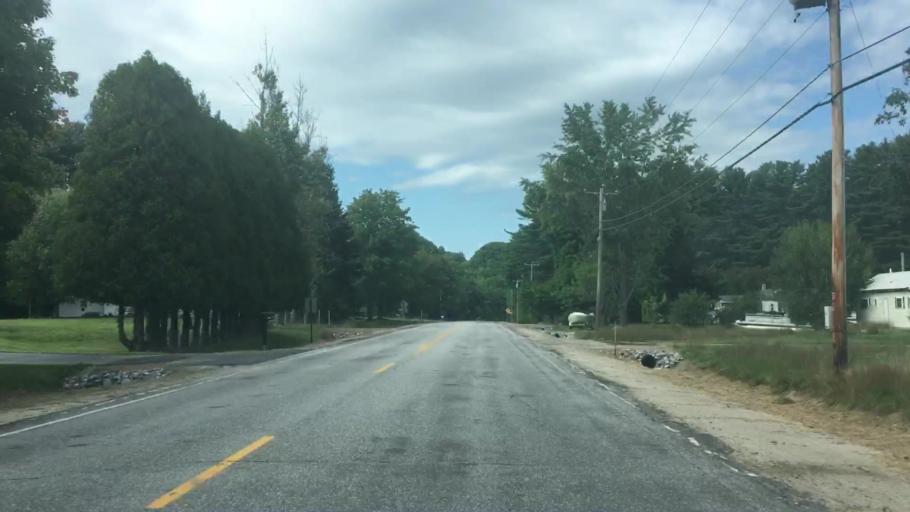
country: US
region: Maine
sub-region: Cumberland County
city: Raymond
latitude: 43.9862
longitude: -70.5193
